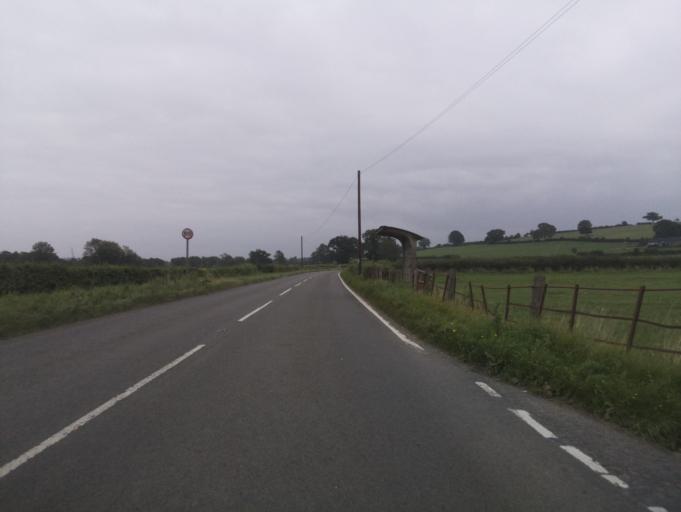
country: GB
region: England
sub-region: Derbyshire
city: Duffield
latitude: 53.0022
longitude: -1.5336
